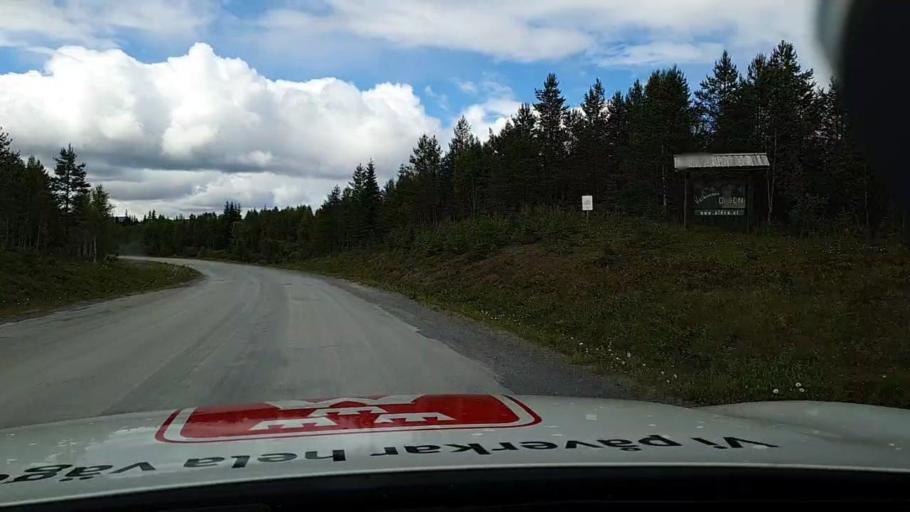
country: SE
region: Jaemtland
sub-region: Krokoms Kommun
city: Valla
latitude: 63.6861
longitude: 13.6827
